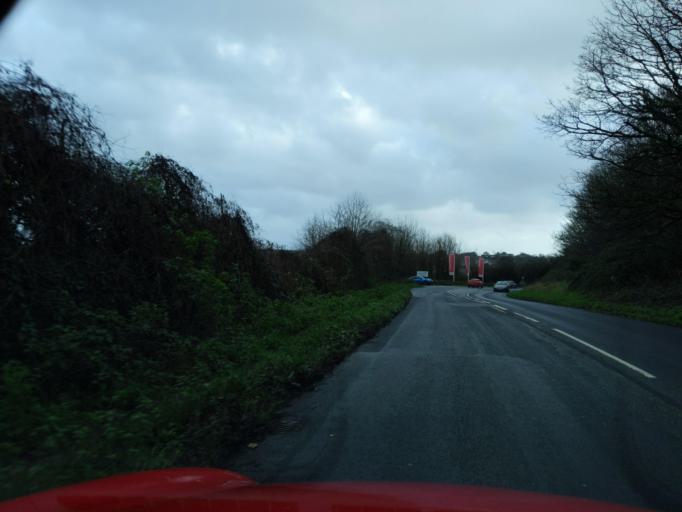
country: GB
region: England
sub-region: Devon
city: Plympton
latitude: 50.3707
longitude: -4.0683
